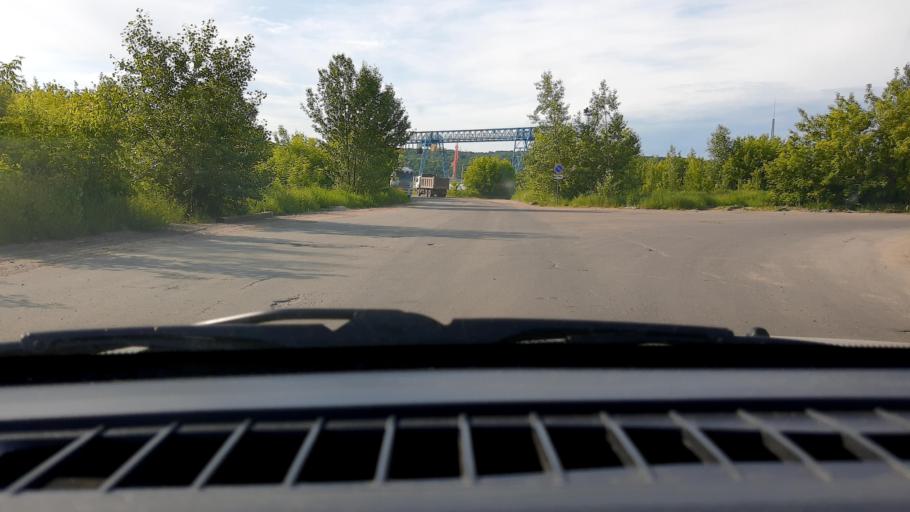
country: RU
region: Nizjnij Novgorod
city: Nizhniy Novgorod
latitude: 56.2365
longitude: 43.9092
